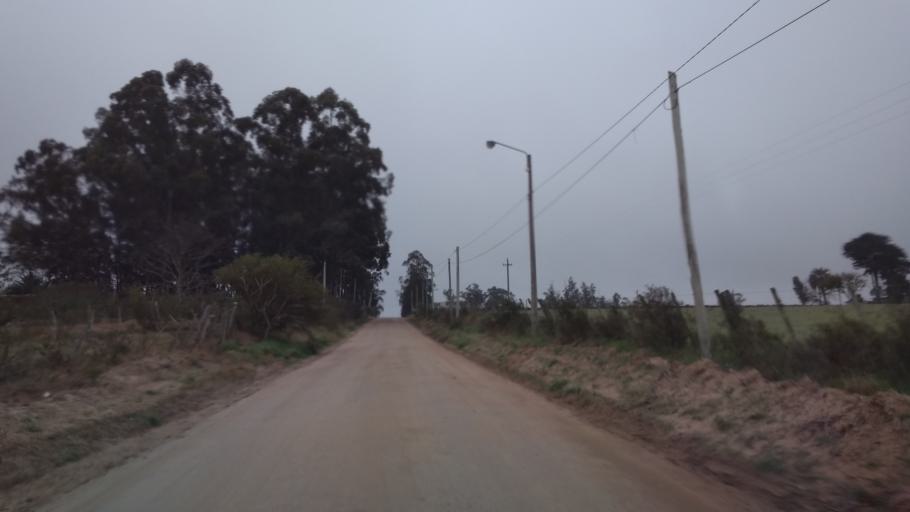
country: UY
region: Florida
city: Florida
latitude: -34.0804
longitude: -56.2033
